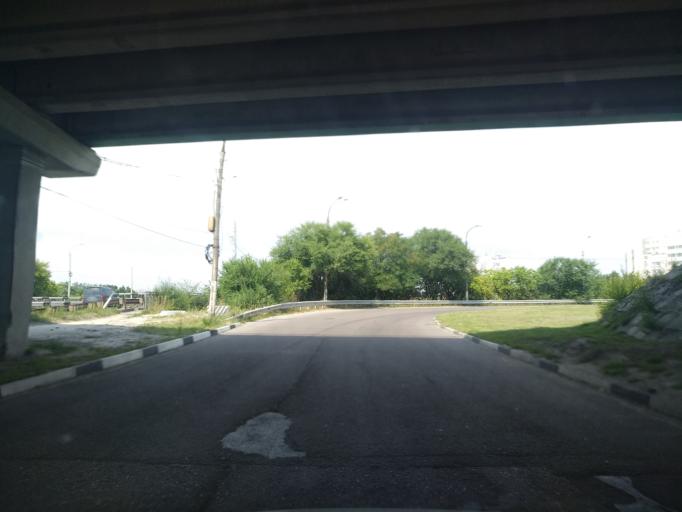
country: RU
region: Voronezj
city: Voronezh
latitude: 51.6952
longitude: 39.2281
